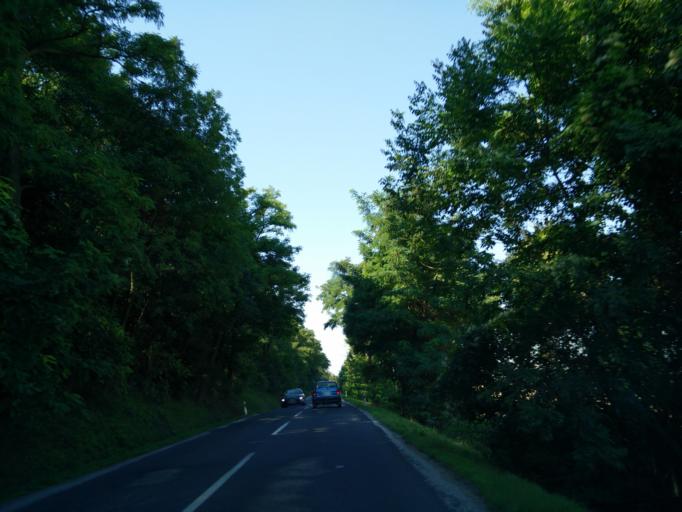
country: SK
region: Nitriansky
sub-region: Okres Nitra
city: Nitra
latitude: 48.3693
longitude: 18.0800
